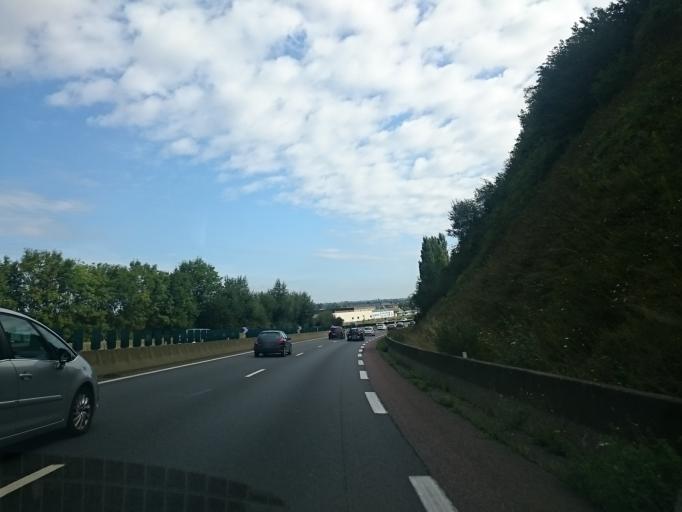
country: FR
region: Lower Normandy
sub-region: Departement de la Manche
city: Avranches
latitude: 48.6868
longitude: -1.3741
